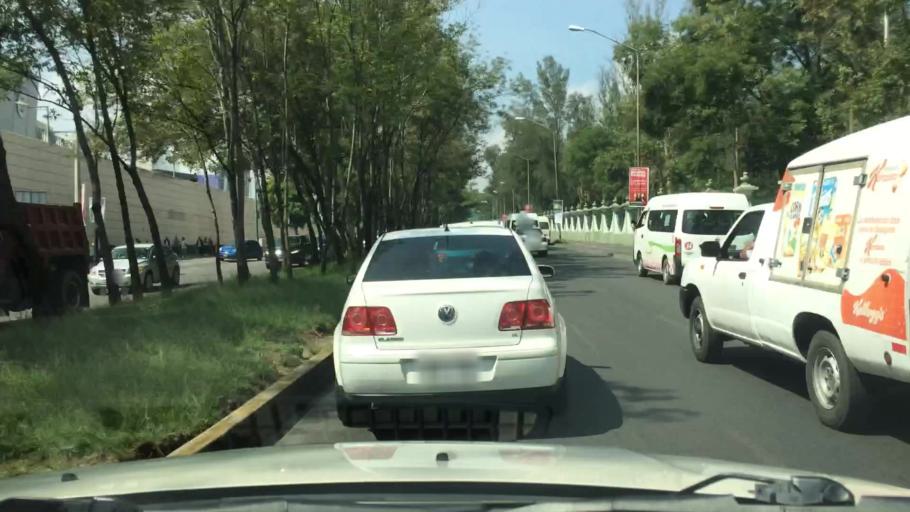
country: MX
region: Mexico City
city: Miguel Hidalgo
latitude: 19.4417
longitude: -99.2236
